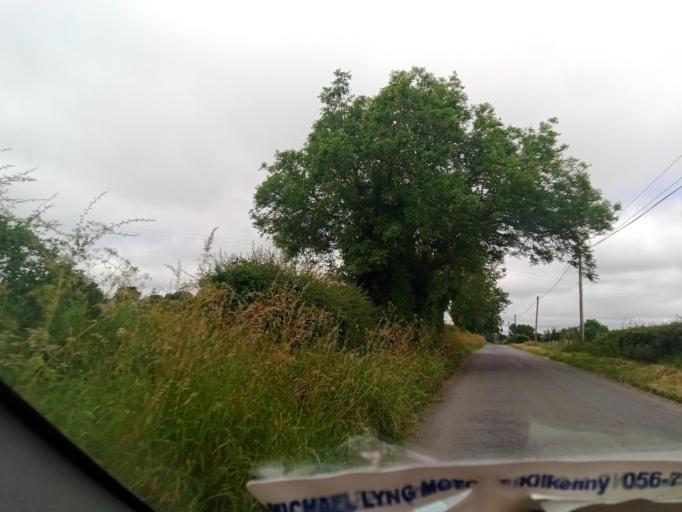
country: IE
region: Leinster
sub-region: Kilkenny
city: Ballyragget
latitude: 52.7542
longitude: -7.4437
